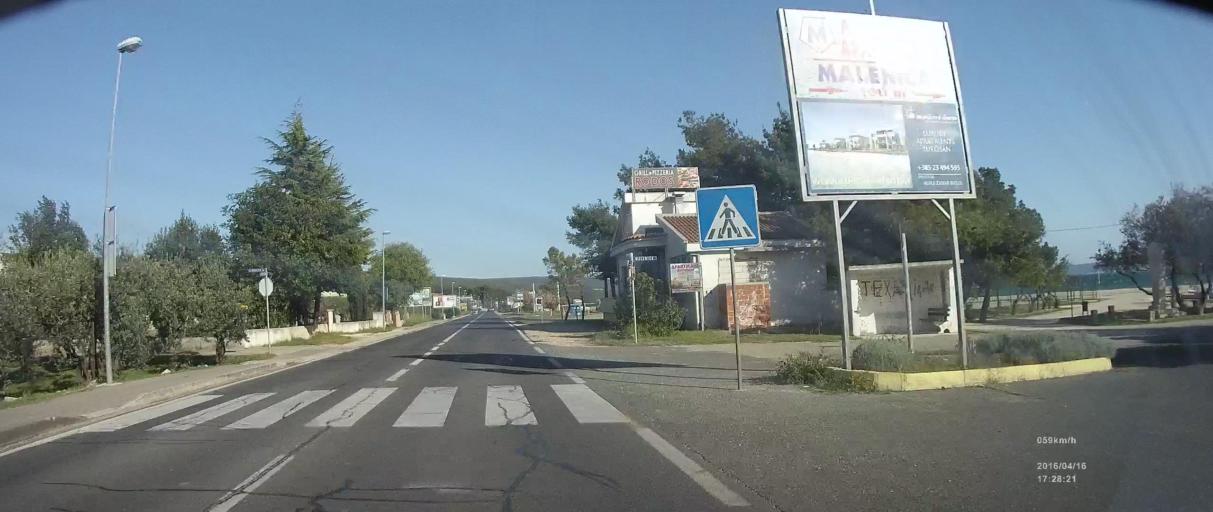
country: HR
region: Zadarska
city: Sukosan
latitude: 44.0370
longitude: 15.3293
